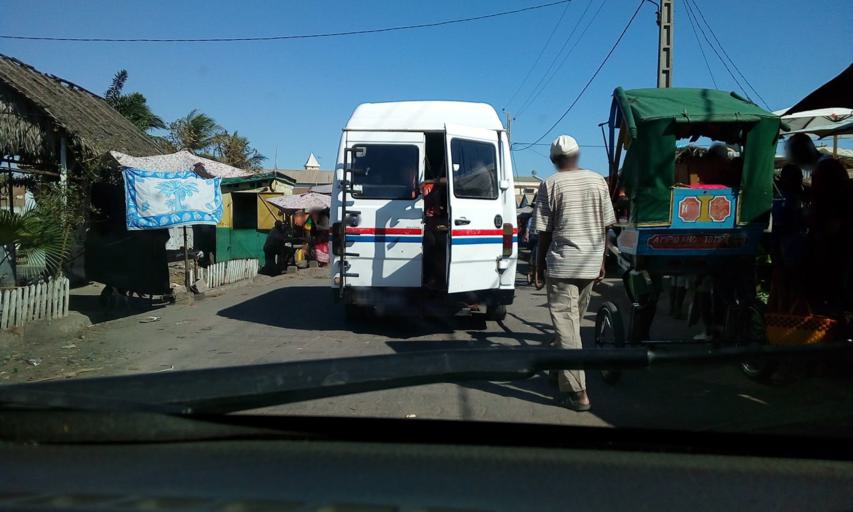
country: MG
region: Boeny
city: Mahajanga
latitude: -15.7092
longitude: 46.3265
